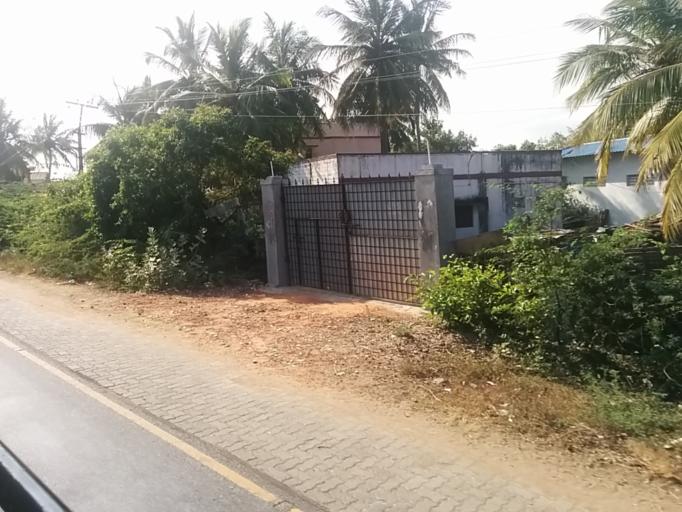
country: IN
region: Tamil Nadu
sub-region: Kancheepuram
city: Mamallapuram
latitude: 12.6183
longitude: 80.1776
